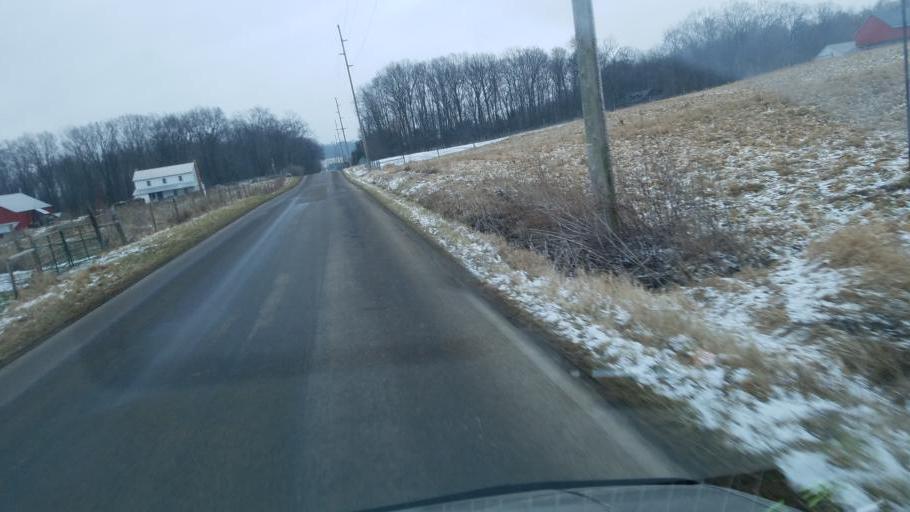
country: US
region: Ohio
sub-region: Wayne County
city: Apple Creek
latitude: 40.7110
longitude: -81.8896
